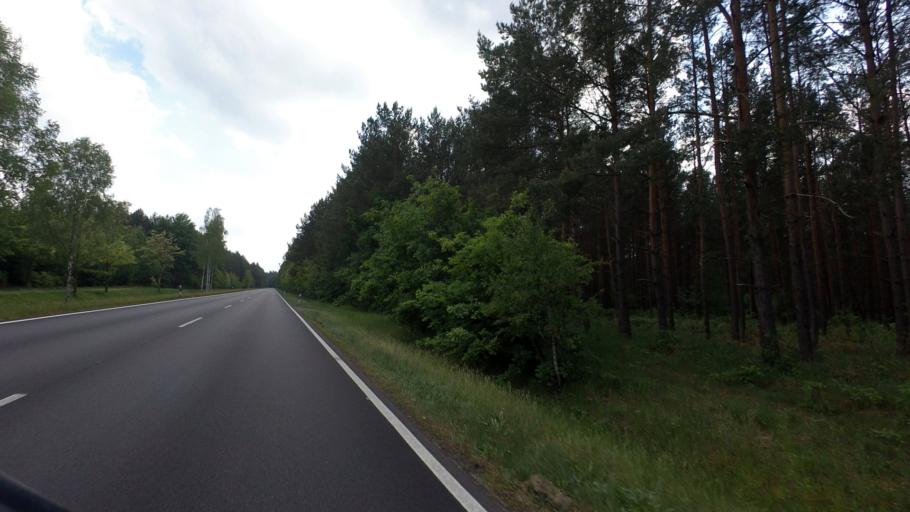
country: DE
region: Saxony
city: Rietschen
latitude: 51.3802
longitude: 14.7888
